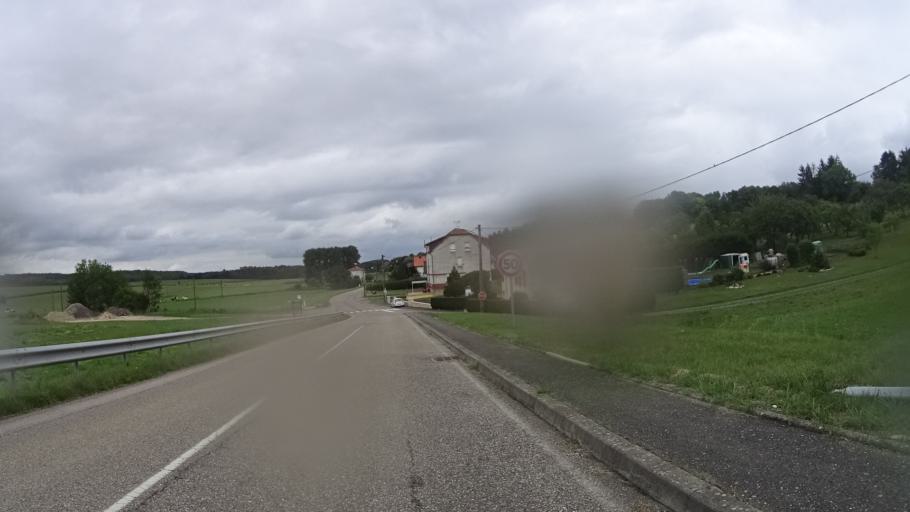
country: FR
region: Lorraine
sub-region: Departement de la Moselle
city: Dieuze
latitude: 48.6790
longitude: 6.7897
